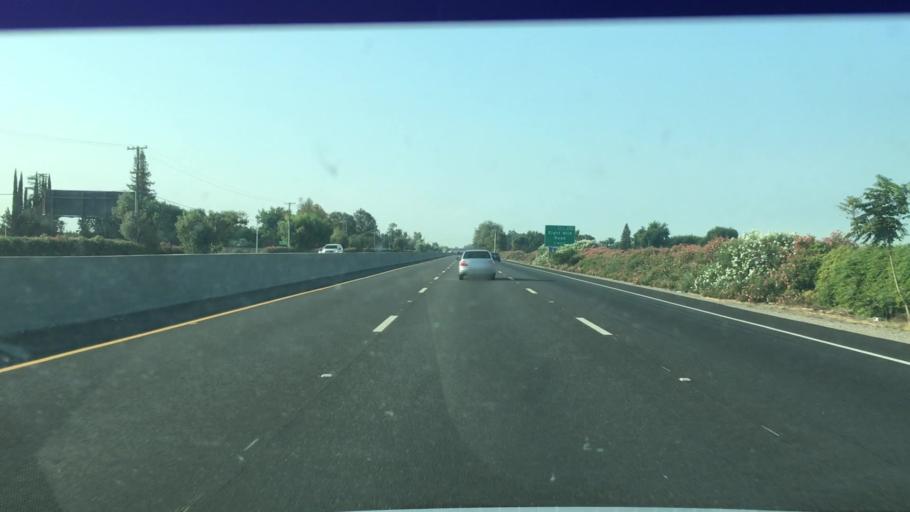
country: US
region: California
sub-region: San Joaquin County
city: Morada
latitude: 38.0726
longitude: -121.2599
